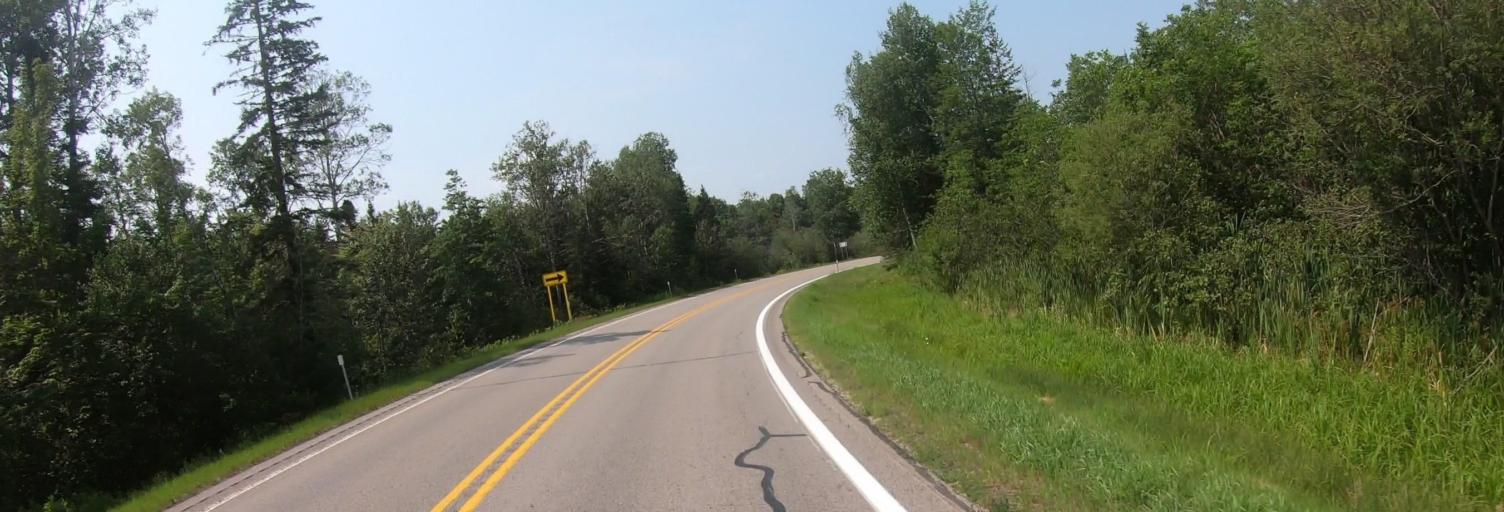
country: US
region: Michigan
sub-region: Luce County
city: Newberry
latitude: 46.5647
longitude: -85.2891
